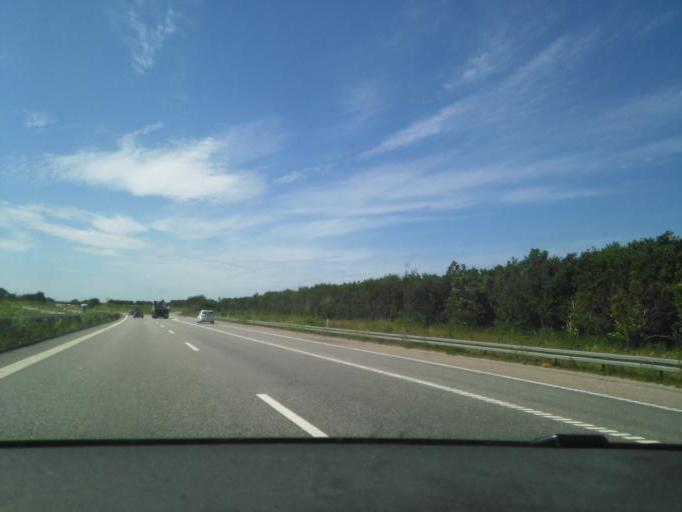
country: DK
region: Zealand
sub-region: Roskilde Kommune
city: Roskilde
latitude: 55.6264
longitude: 12.0515
